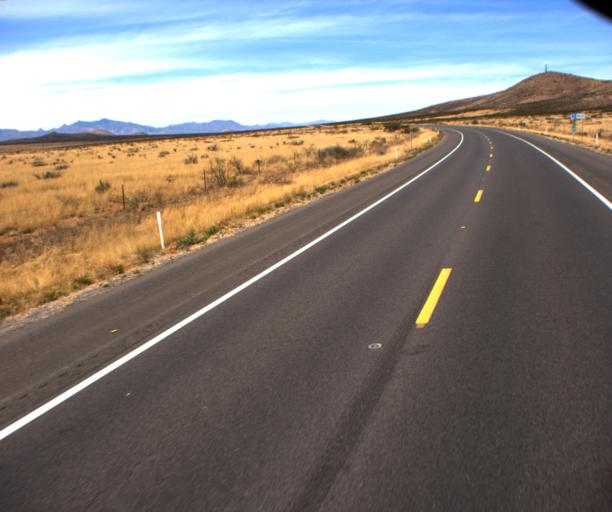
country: US
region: Arizona
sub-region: Cochise County
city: Willcox
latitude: 31.8949
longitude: -109.6980
